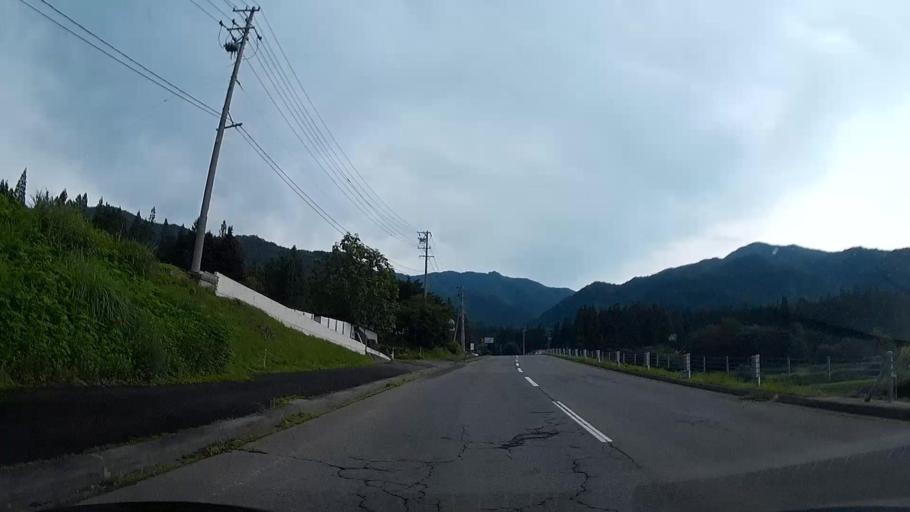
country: JP
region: Nagano
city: Nakano
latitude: 36.7254
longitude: 138.4449
